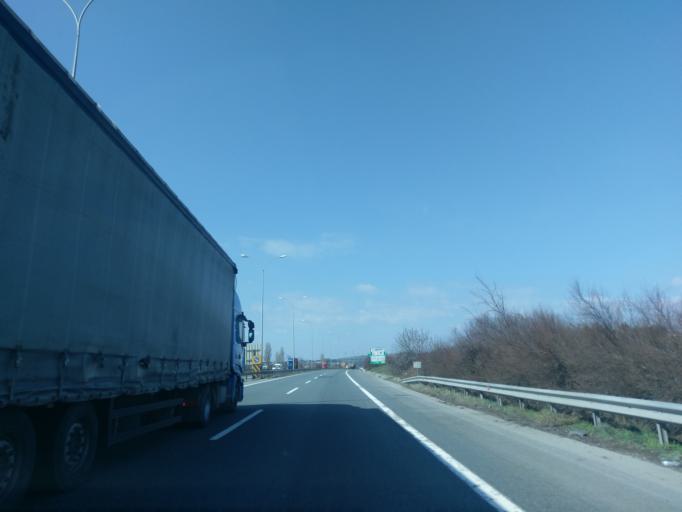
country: TR
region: Istanbul
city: Selimpasa
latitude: 41.0744
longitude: 28.3777
